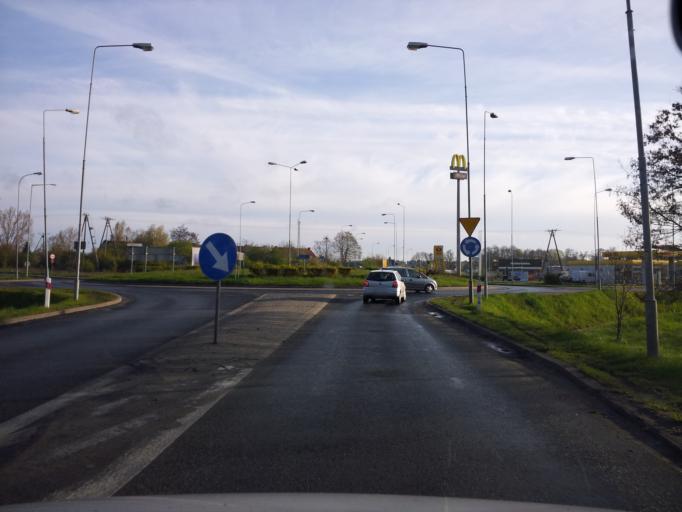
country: PL
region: Lubusz
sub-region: Powiat zarski
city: Zary
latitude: 51.6341
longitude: 15.1179
